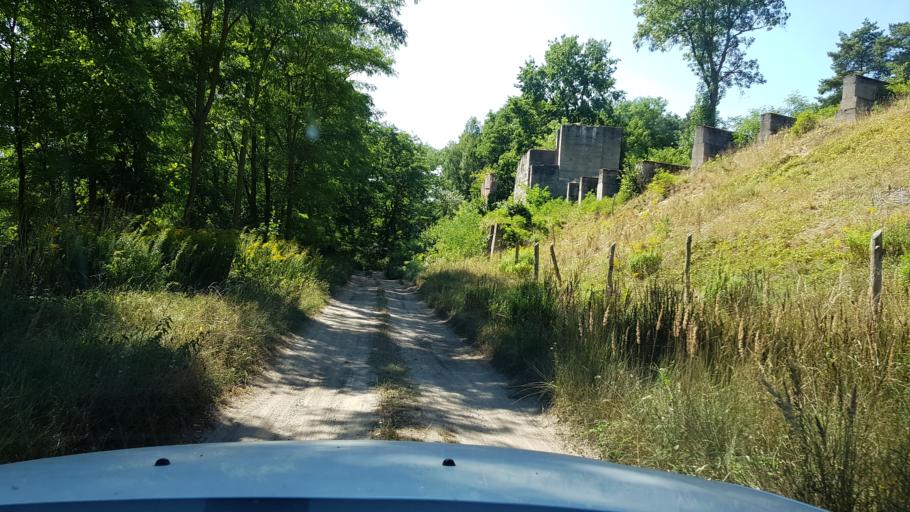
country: PL
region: West Pomeranian Voivodeship
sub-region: Powiat gryfinski
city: Cedynia
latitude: 52.8336
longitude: 14.2501
